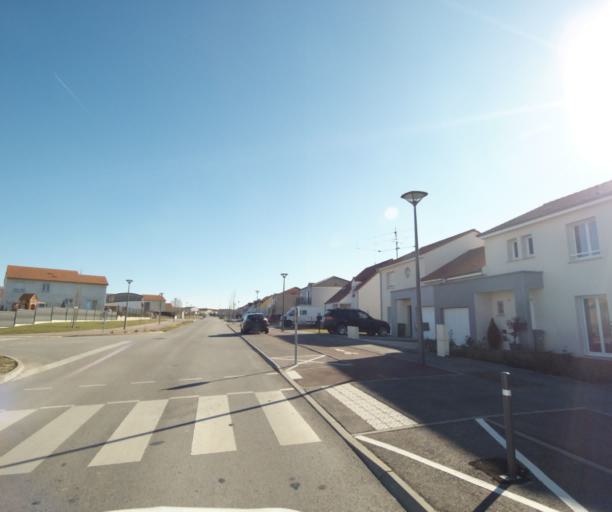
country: FR
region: Lorraine
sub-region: Departement de Meurthe-et-Moselle
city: Tomblaine
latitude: 48.6782
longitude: 6.2278
